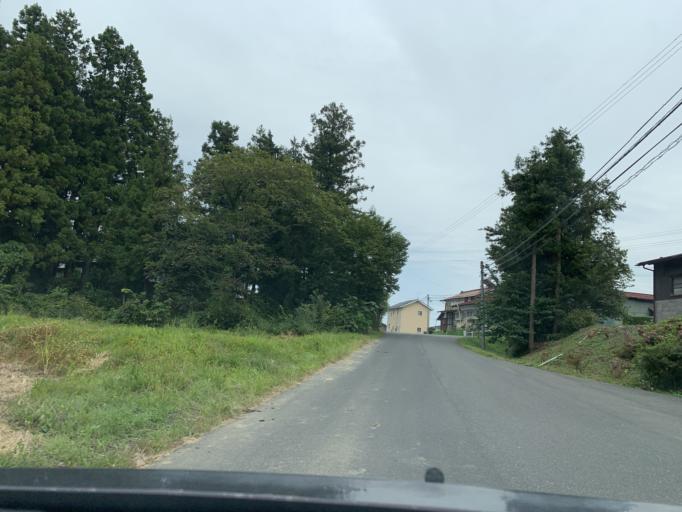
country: JP
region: Iwate
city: Ichinoseki
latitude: 38.9564
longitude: 141.1276
